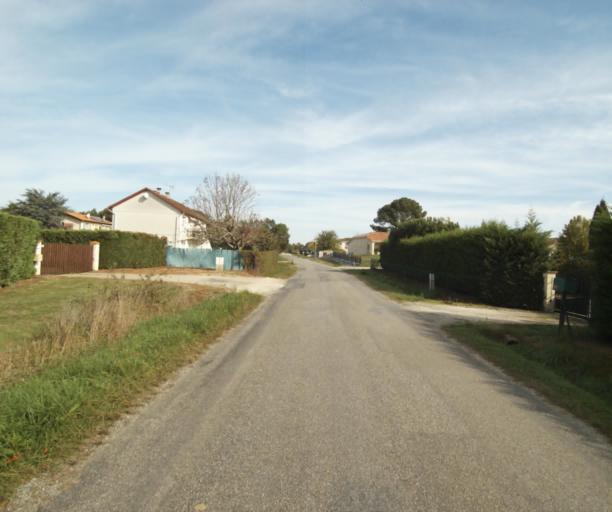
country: FR
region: Midi-Pyrenees
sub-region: Departement du Tarn-et-Garonne
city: Orgueil
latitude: 43.8954
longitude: 1.4073
